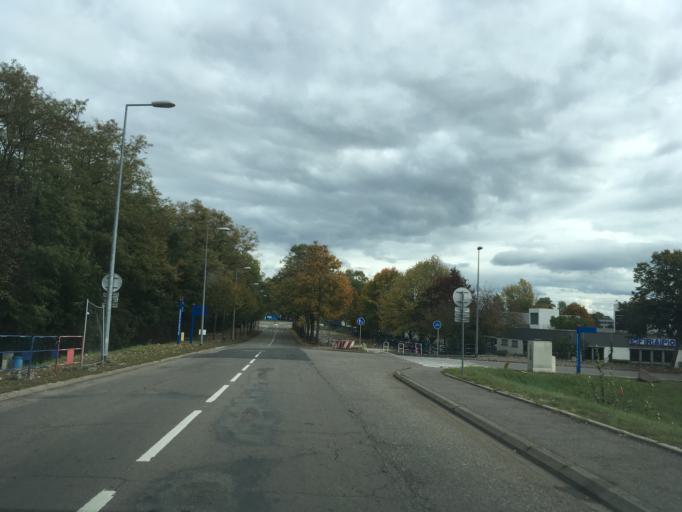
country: DE
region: Baden-Wuerttemberg
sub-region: Freiburg Region
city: Kehl
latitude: 48.5448
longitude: 7.7836
